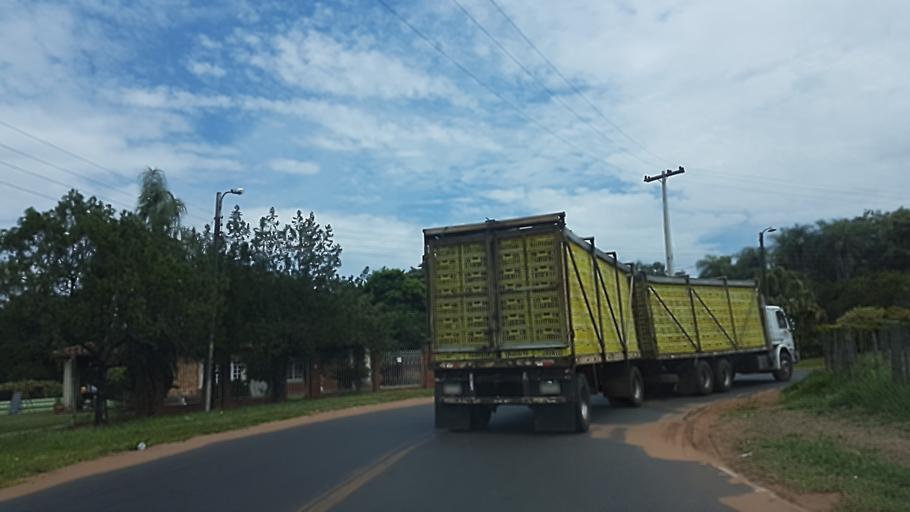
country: PY
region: Central
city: San Lorenzo
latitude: -25.3099
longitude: -57.4686
